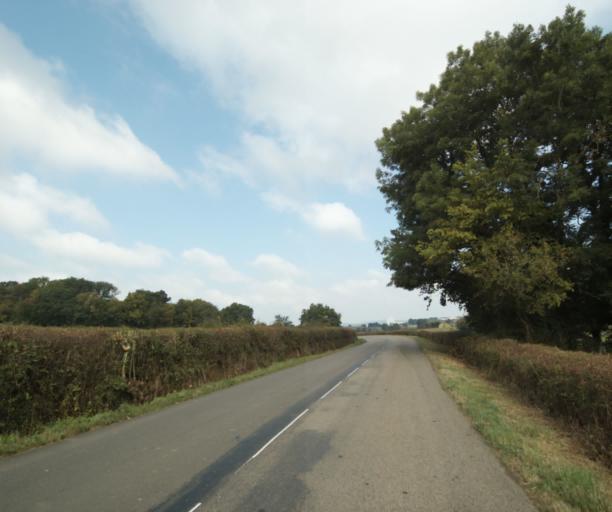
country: FR
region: Bourgogne
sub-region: Departement de Saone-et-Loire
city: Charolles
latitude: 46.4255
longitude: 4.3068
